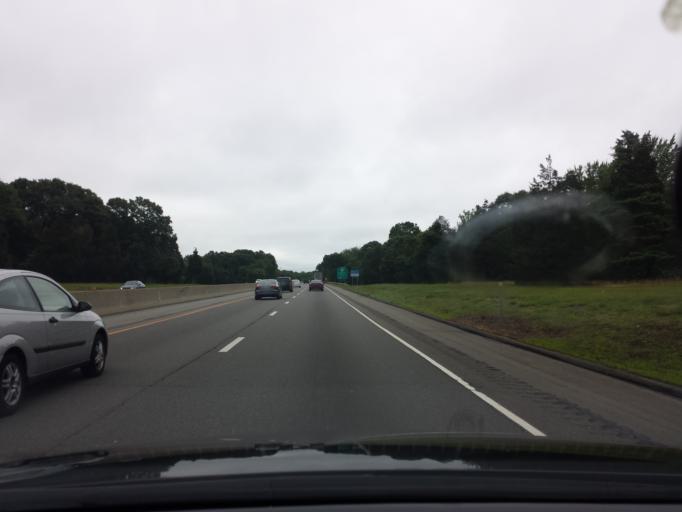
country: US
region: Connecticut
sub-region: New Haven County
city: Madison Center
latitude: 41.2880
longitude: -72.6178
